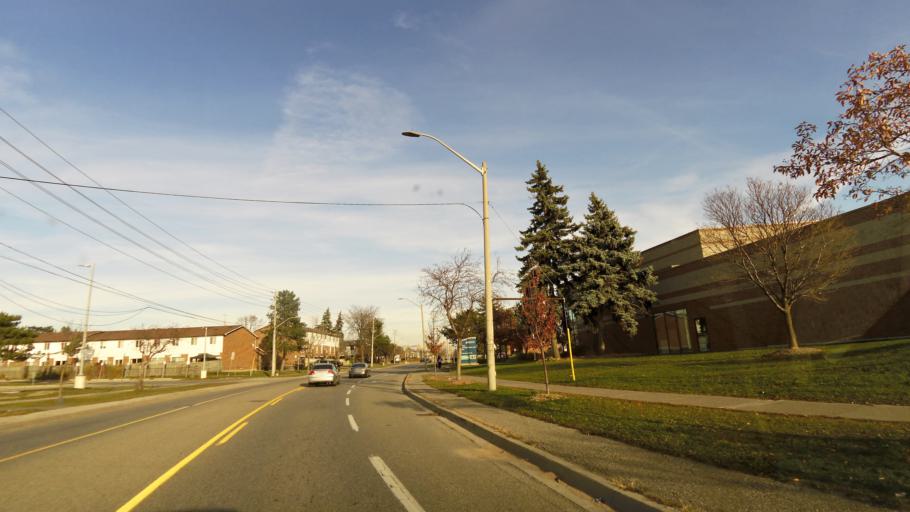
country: CA
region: Ontario
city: Etobicoke
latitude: 43.7237
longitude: -79.6396
